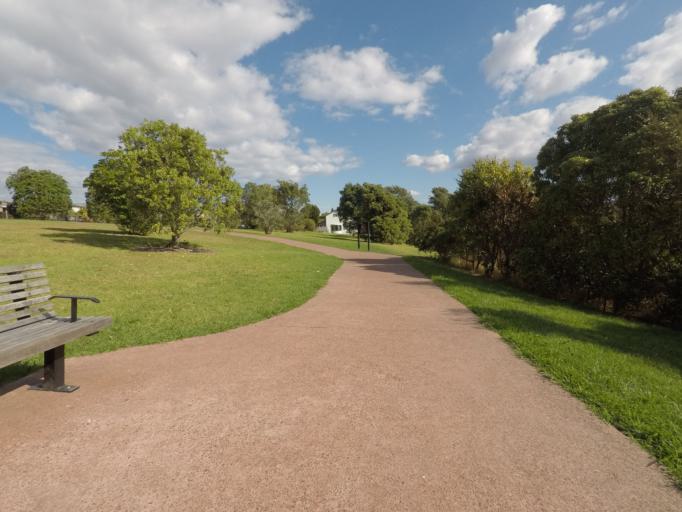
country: NZ
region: Auckland
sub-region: Auckland
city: Rosebank
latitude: -36.8853
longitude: 174.6950
